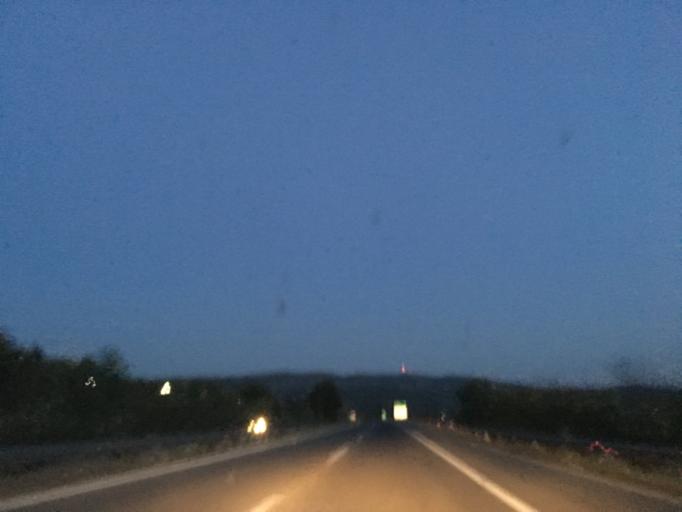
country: MK
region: Petrovec
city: Petrovec
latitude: 41.8972
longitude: 21.6674
